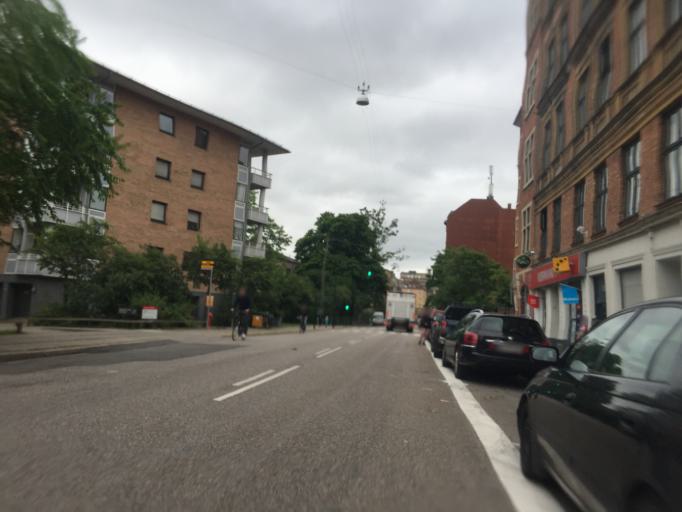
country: DK
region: Capital Region
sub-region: Kobenhavn
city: Copenhagen
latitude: 55.6765
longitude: 12.5538
